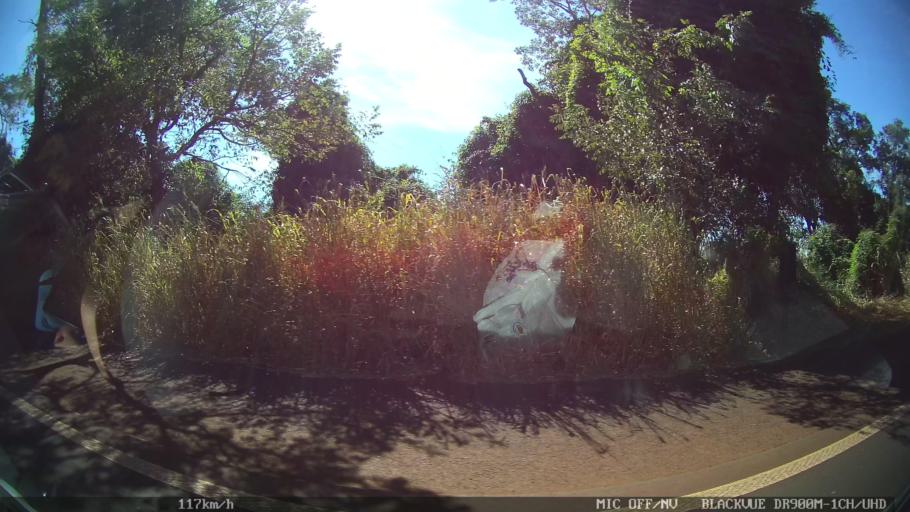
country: BR
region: Sao Paulo
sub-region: Guaira
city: Guaira
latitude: -20.4435
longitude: -48.3238
